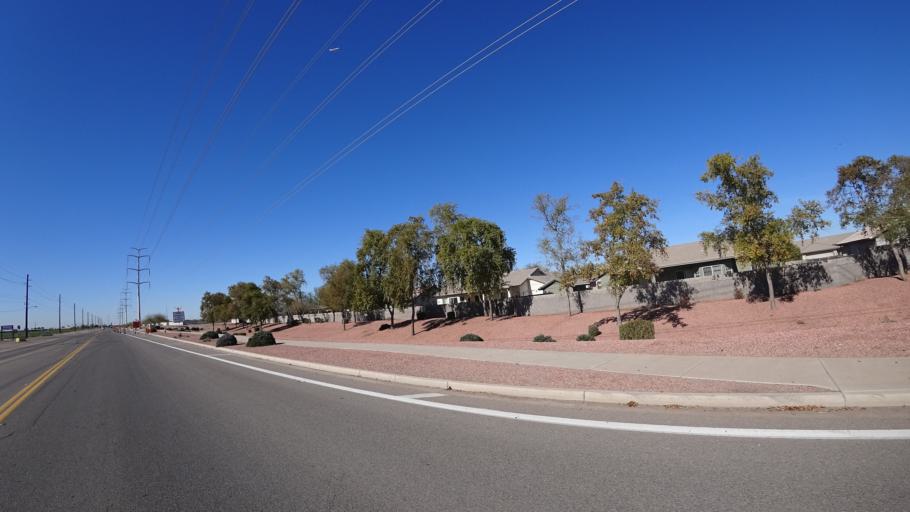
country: US
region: Arizona
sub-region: Maricopa County
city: Tolleson
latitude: 33.4085
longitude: -112.2277
